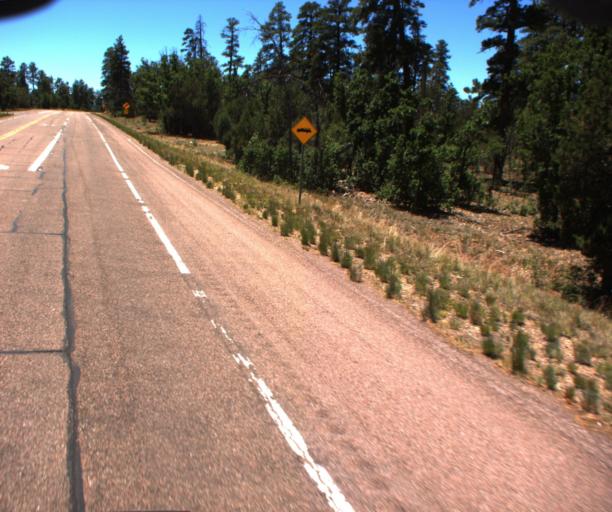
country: US
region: Arizona
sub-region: Gila County
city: Star Valley
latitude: 34.6376
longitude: -111.1106
